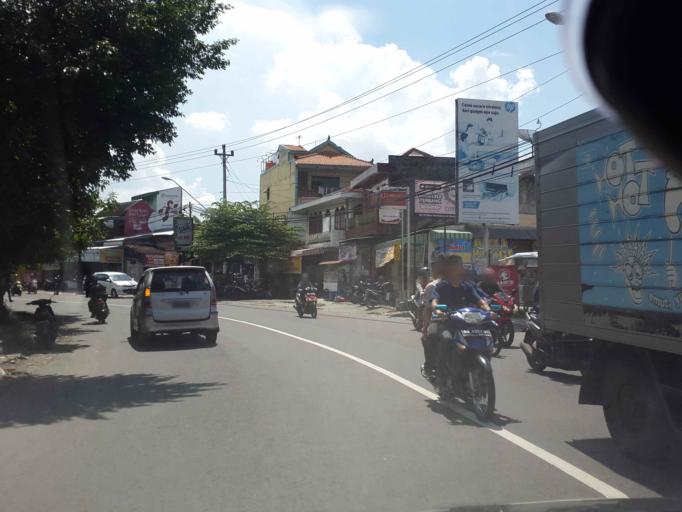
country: ID
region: Central Java
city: Surakarta
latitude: -7.5543
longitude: 110.8571
